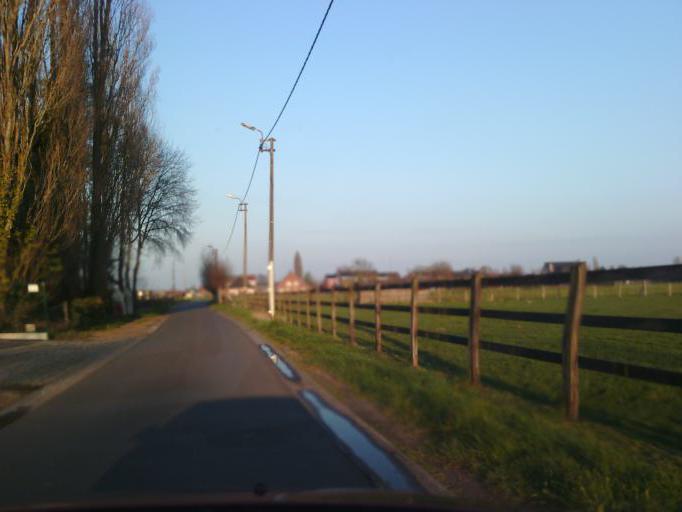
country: BE
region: Flanders
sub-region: Provincie Oost-Vlaanderen
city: Berlare
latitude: 51.0547
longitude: 3.9503
